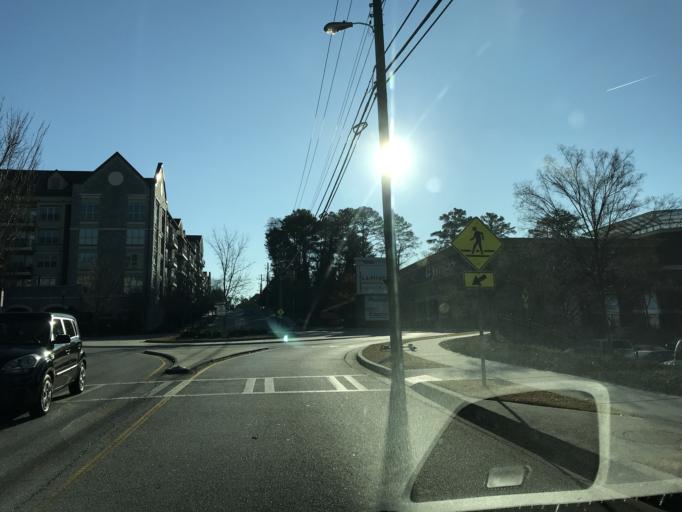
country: US
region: Georgia
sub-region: DeKalb County
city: North Atlanta
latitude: 33.8731
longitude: -84.3352
